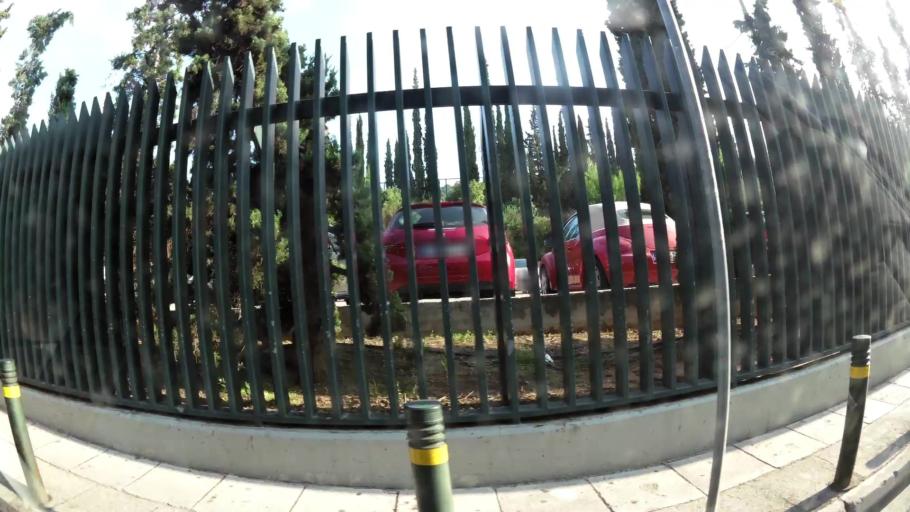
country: GR
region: Attica
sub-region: Nomarchia Athinas
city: Agia Paraskevi
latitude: 38.0041
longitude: 23.8311
